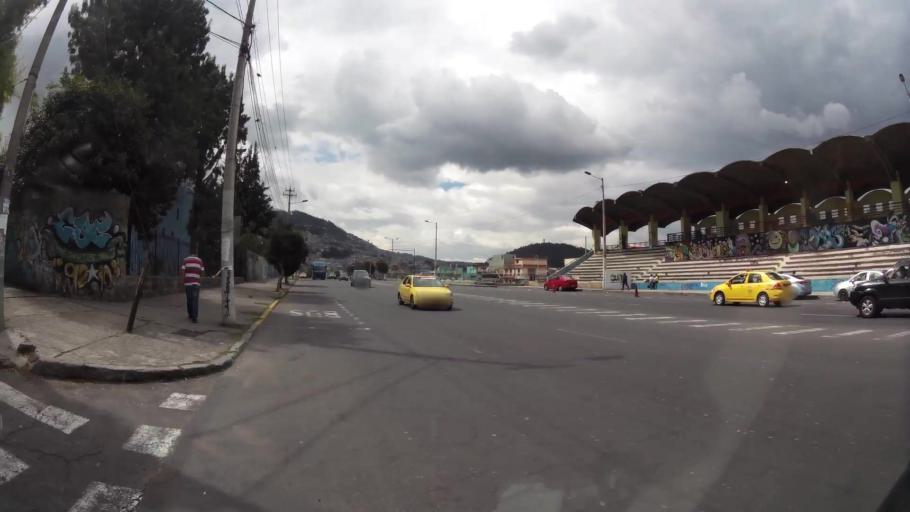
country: EC
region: Pichincha
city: Quito
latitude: -0.2480
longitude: -78.5310
